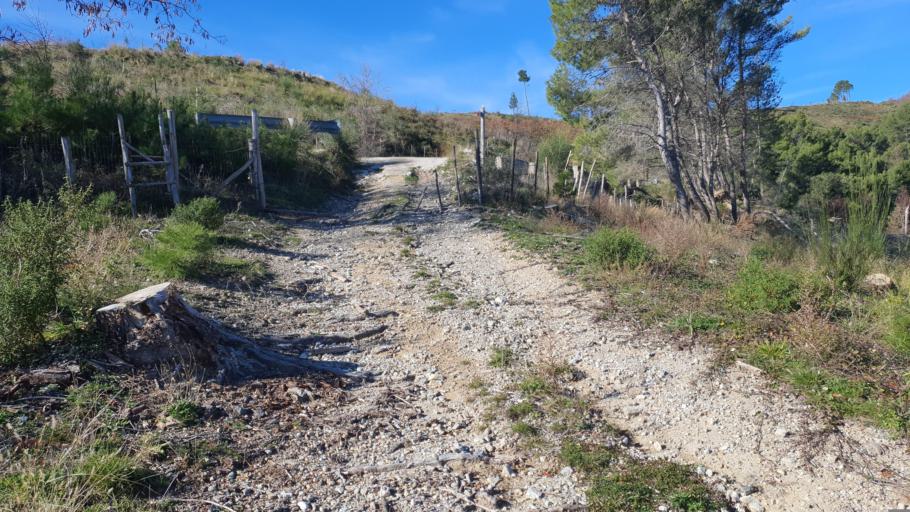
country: IT
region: Calabria
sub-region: Provincia di Catanzaro
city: Zagarise
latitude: 39.0121
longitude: 16.6843
